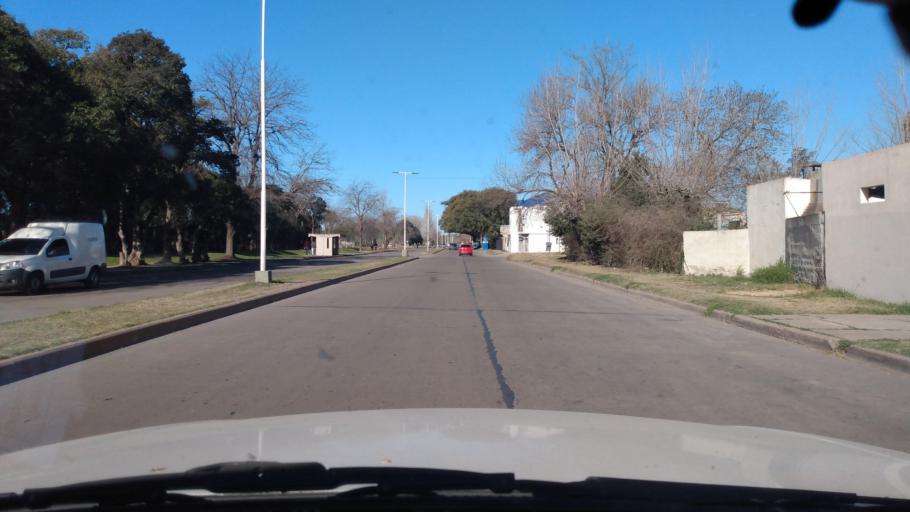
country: AR
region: Buenos Aires
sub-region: Partido de Mercedes
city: Mercedes
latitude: -34.6482
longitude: -59.4124
